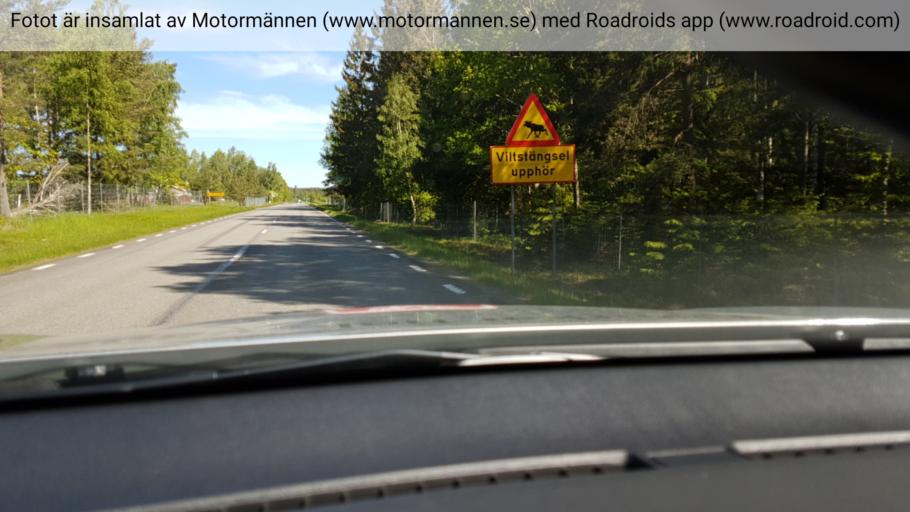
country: SE
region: Vaestra Goetaland
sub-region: Hjo Kommun
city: Hjo
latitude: 58.3793
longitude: 14.3514
